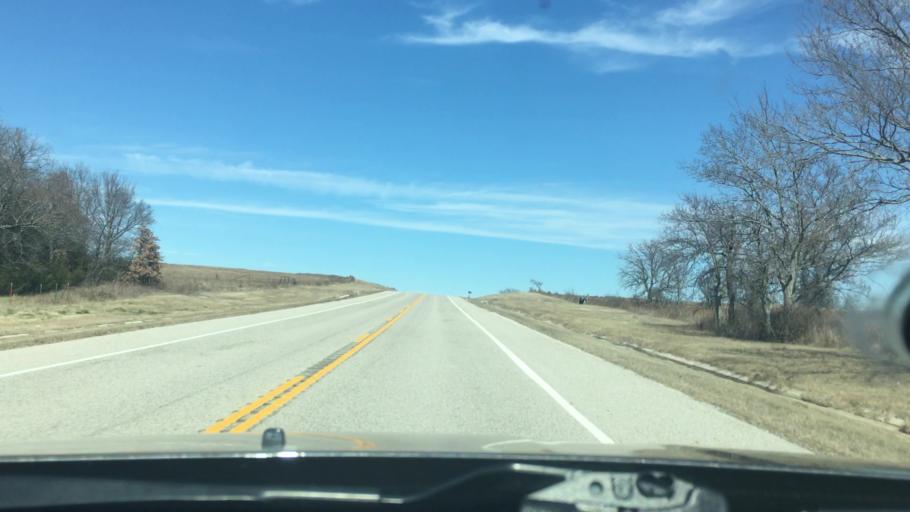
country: US
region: Oklahoma
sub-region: Carter County
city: Dickson
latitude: 34.3386
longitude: -96.9509
